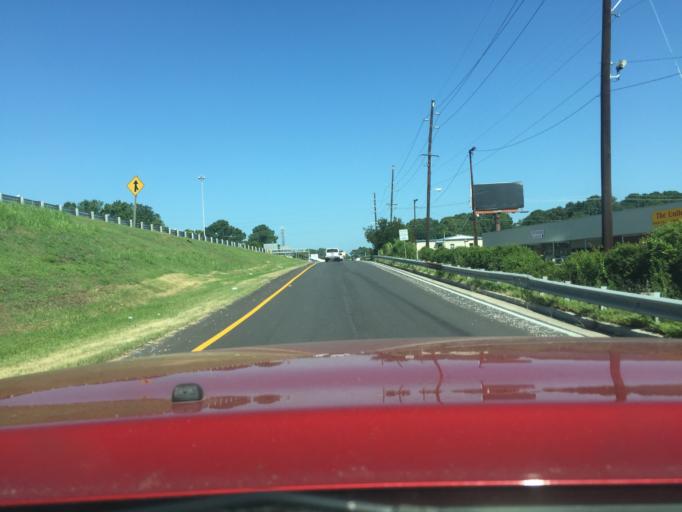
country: US
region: Georgia
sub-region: Chatham County
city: Garden City
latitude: 32.0999
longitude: -81.1431
